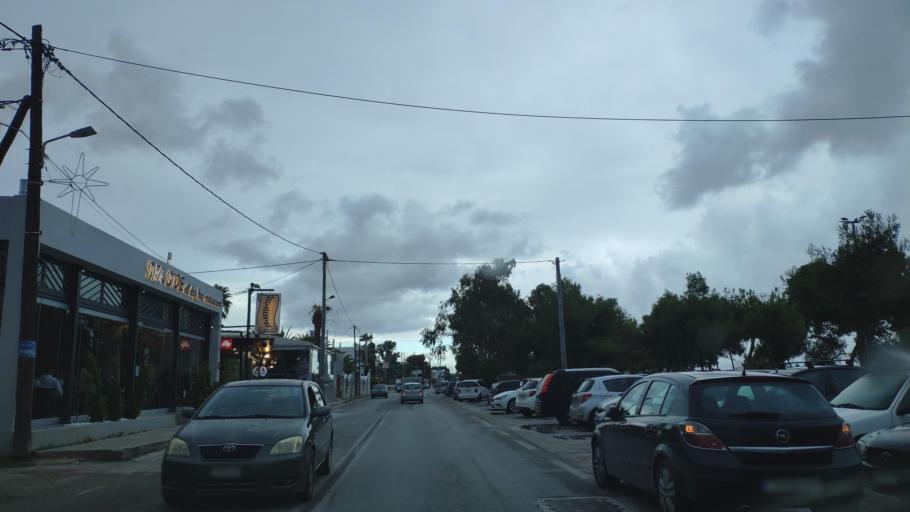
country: GR
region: Attica
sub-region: Nomarchia Anatolikis Attikis
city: Artemida
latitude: 37.9818
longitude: 24.0097
